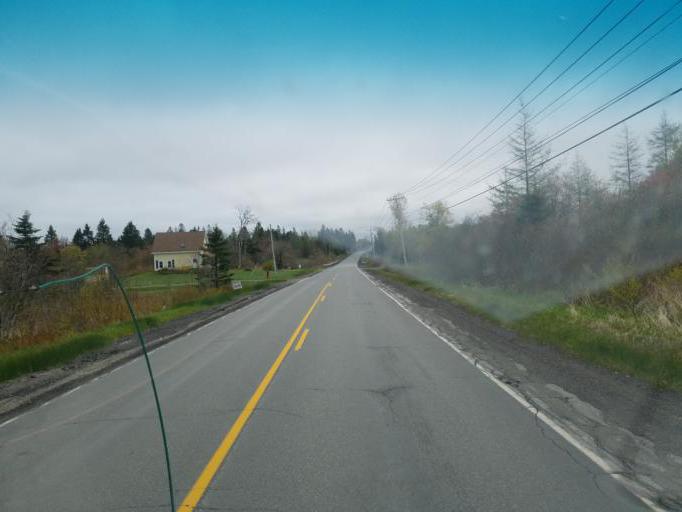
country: US
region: Maine
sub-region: Washington County
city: Eastport
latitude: 44.8288
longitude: -67.0396
